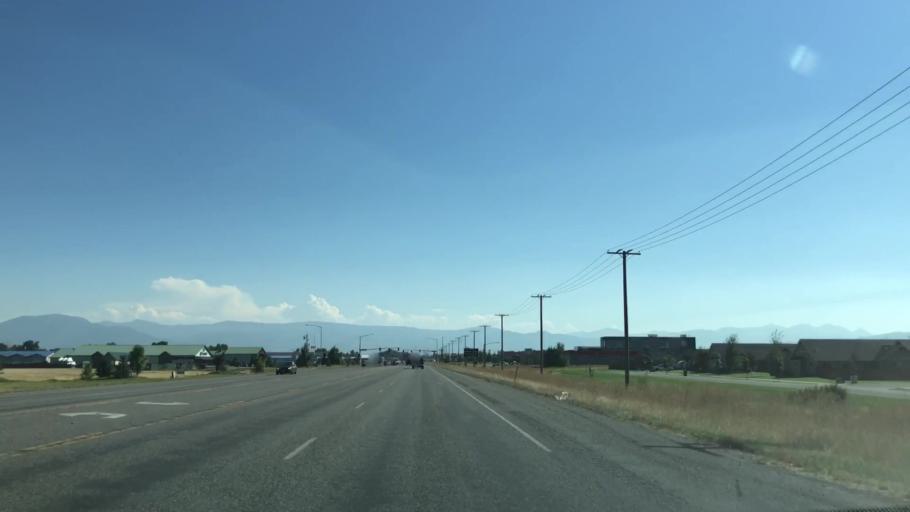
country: US
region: Montana
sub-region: Gallatin County
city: Four Corners
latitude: 45.6821
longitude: -111.1859
